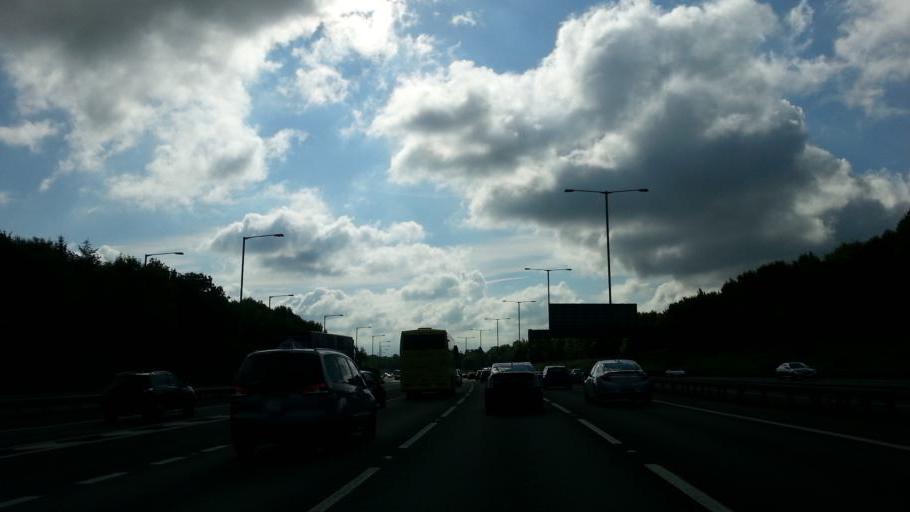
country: GB
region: England
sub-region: Buckinghamshire
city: Denham
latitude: 51.5522
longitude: -0.5251
